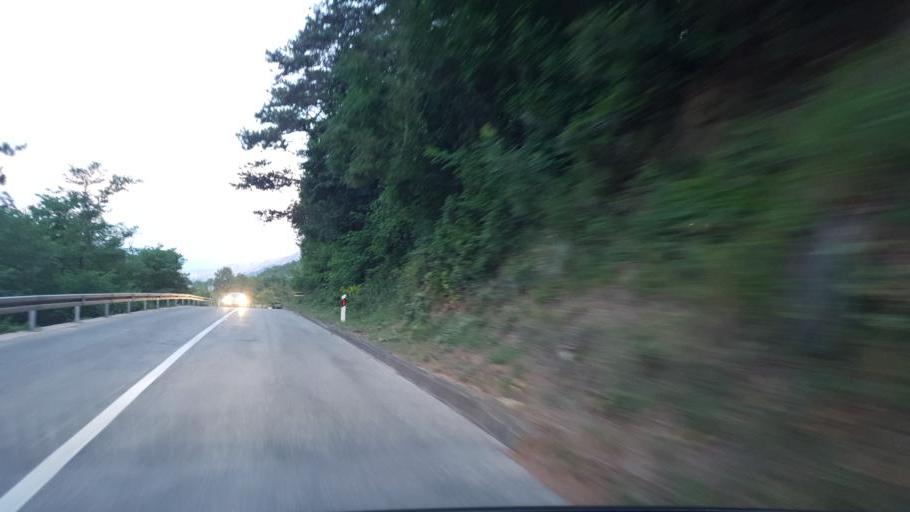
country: HR
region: Primorsko-Goranska
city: Punat
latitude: 45.0085
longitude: 14.7019
